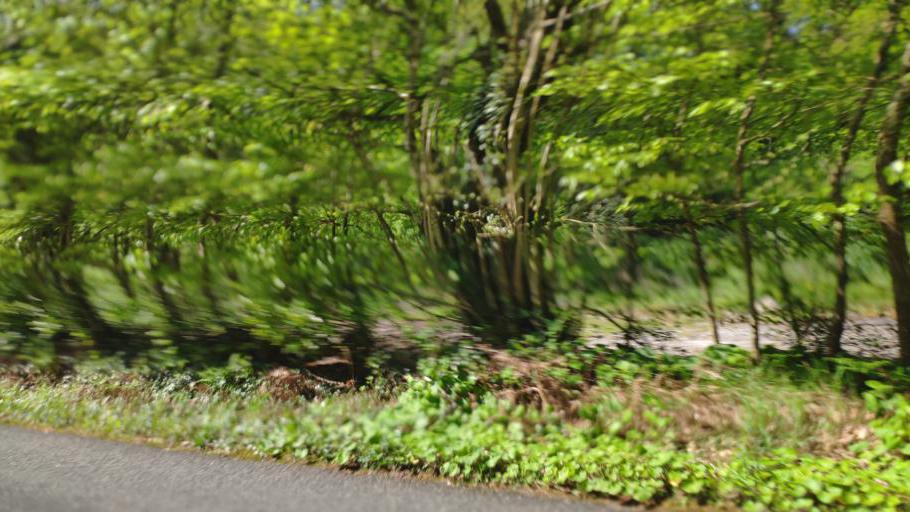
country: IE
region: Munster
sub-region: County Cork
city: Blarney
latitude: 51.9764
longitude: -8.5838
